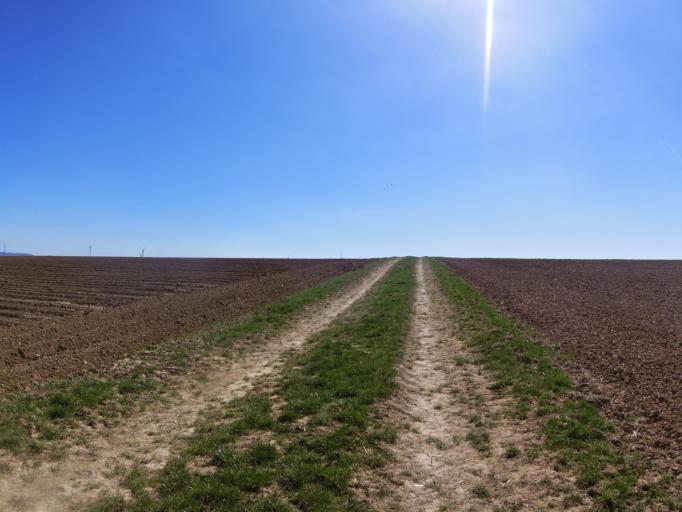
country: DE
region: Bavaria
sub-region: Regierungsbezirk Unterfranken
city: Biebelried
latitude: 49.8029
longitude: 10.0888
